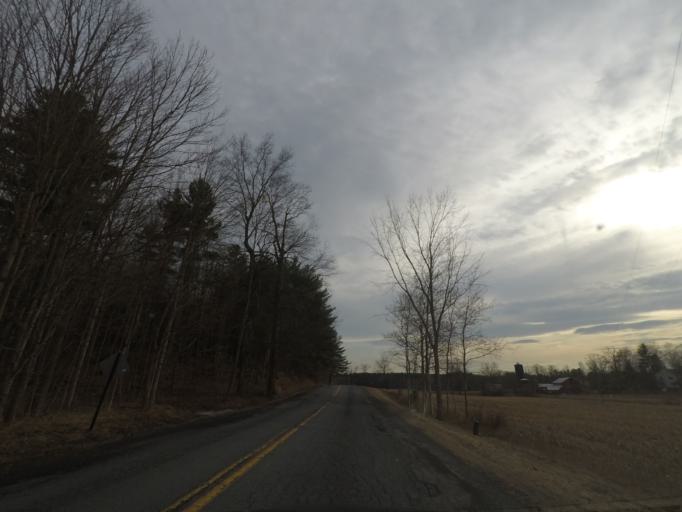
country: US
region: New York
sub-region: Rensselaer County
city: Hoosick Falls
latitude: 42.8739
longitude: -73.4483
